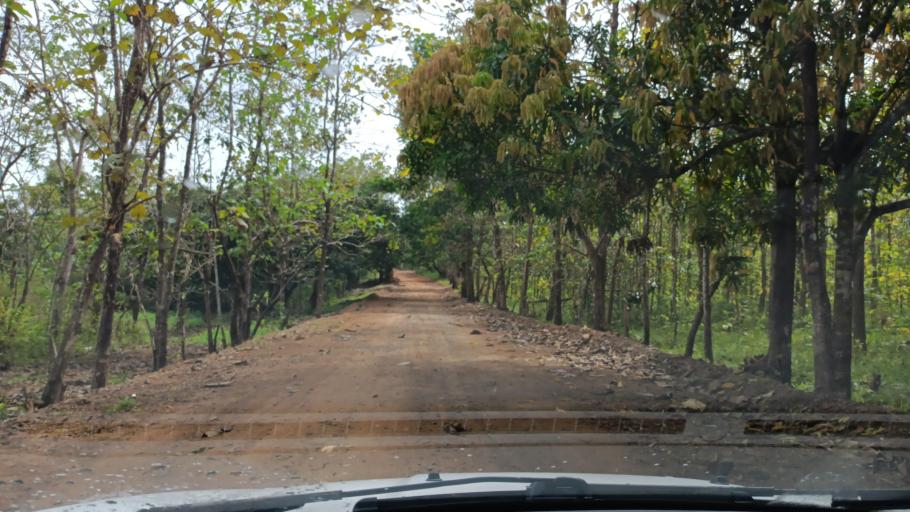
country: PA
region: Panama
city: La Cabima
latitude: 9.1308
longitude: -79.5122
